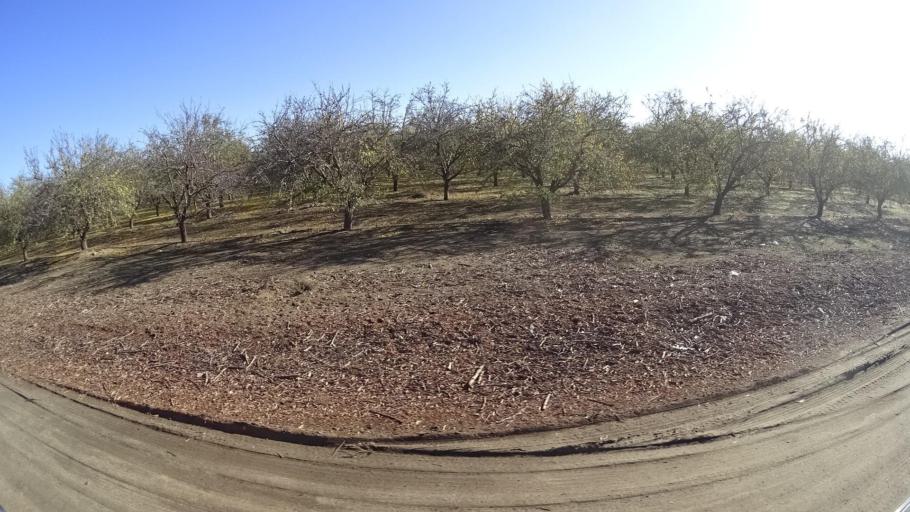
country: US
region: California
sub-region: Kern County
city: McFarland
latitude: 35.6907
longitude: -119.2675
